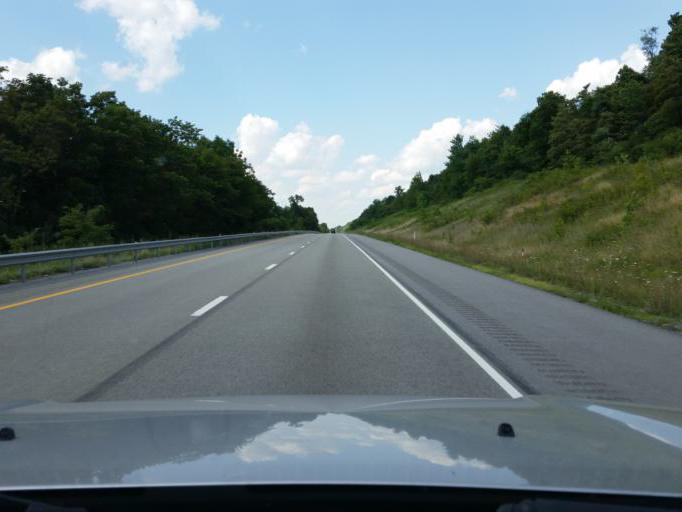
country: US
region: Pennsylvania
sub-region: Blair County
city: Claysburg
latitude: 40.2745
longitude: -78.4512
